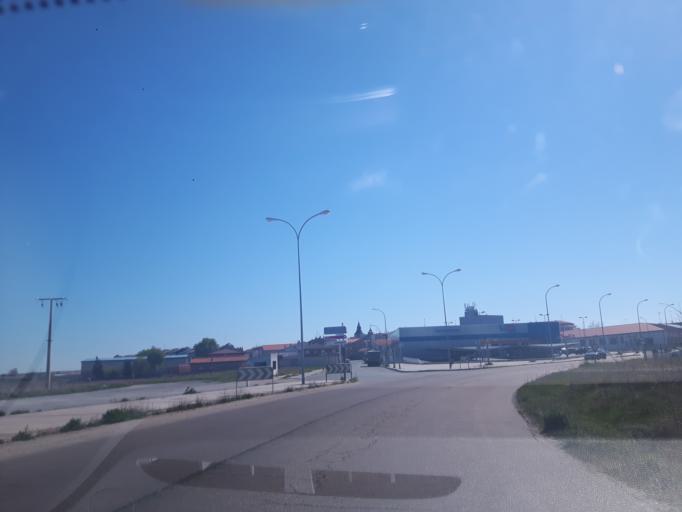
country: ES
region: Castille and Leon
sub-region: Provincia de Salamanca
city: Penaranda de Bracamonte
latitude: 40.9046
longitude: -5.2075
